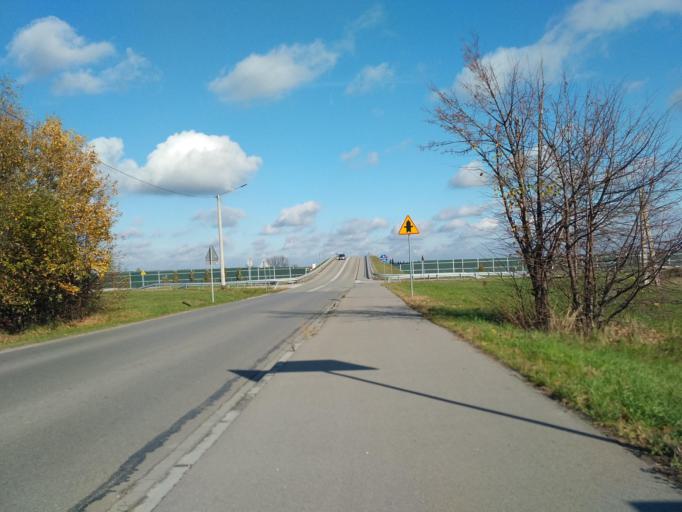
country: PL
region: Subcarpathian Voivodeship
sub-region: Powiat rzeszowski
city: Trzciana
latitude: 50.1059
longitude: 21.8553
